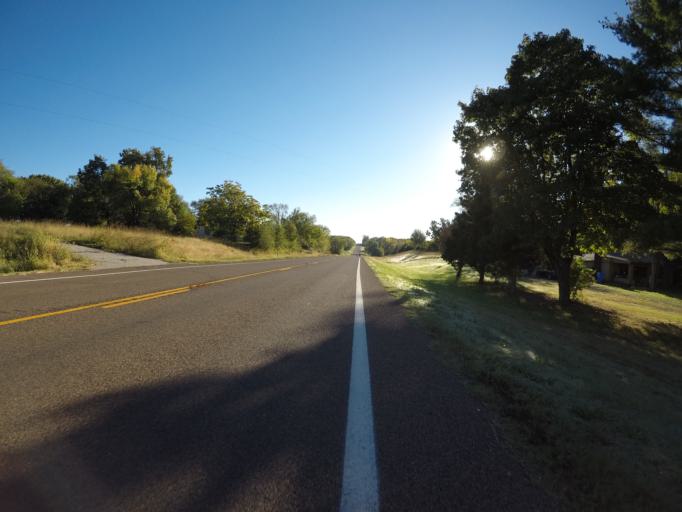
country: US
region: Kansas
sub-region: Douglas County
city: Lawrence
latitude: 39.0005
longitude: -95.1728
